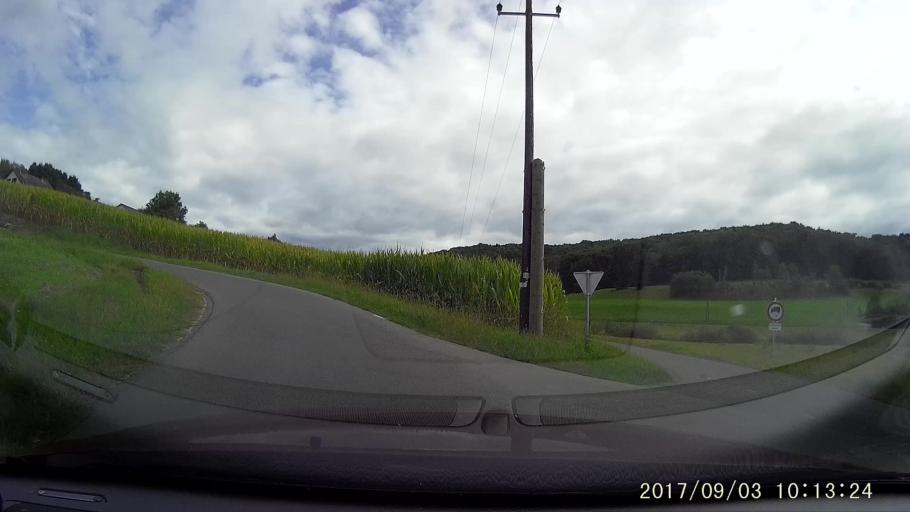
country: AT
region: Styria
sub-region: Politischer Bezirk Suedoststeiermark
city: Auersbach
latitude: 47.0016
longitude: 15.8669
